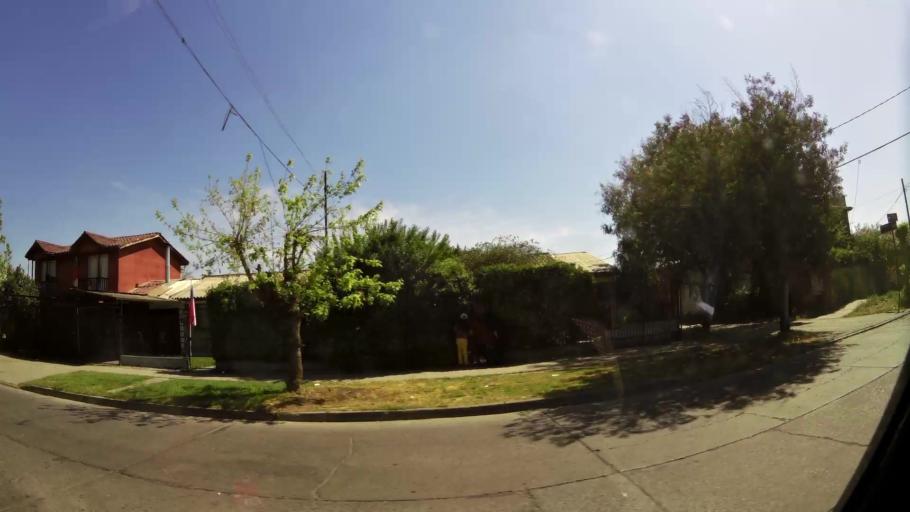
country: CL
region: Santiago Metropolitan
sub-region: Provincia de Santiago
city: Lo Prado
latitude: -33.5123
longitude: -70.7473
